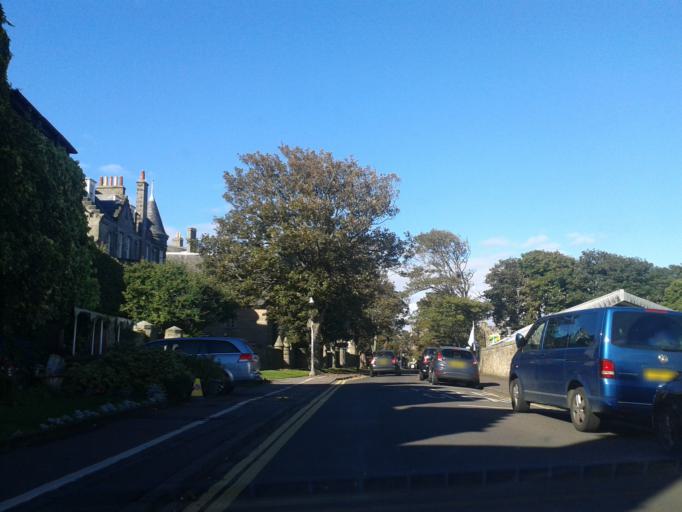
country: GB
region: Scotland
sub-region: Fife
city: Saint Andrews
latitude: 56.3414
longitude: -2.7904
